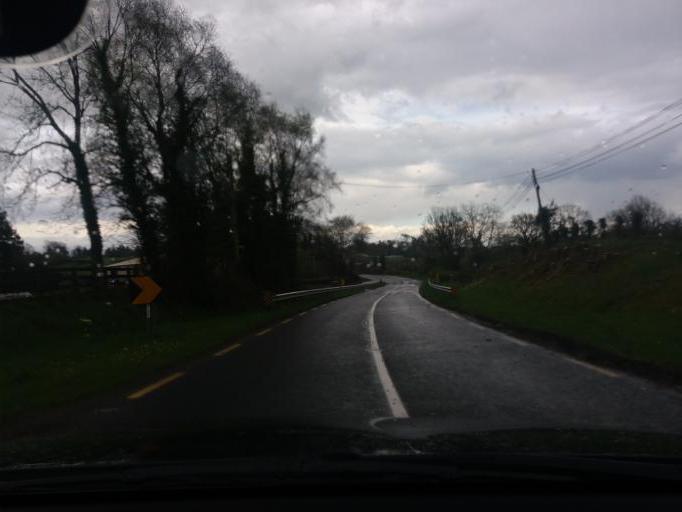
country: IE
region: Ulster
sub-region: An Cabhan
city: Ballyconnell
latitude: 54.1181
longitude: -7.6663
